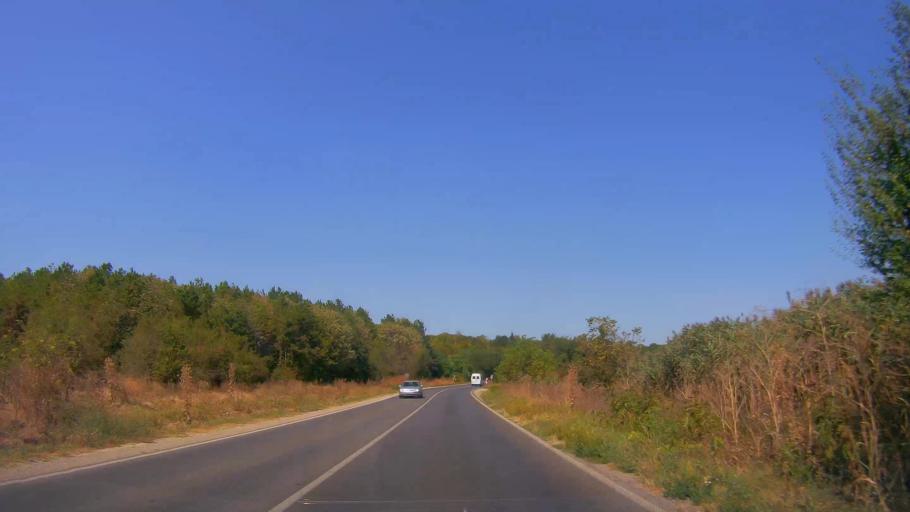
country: BG
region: Razgrad
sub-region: Obshtina Tsar Kaloyan
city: Tsar Kaloyan
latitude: 43.6206
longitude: 26.2118
